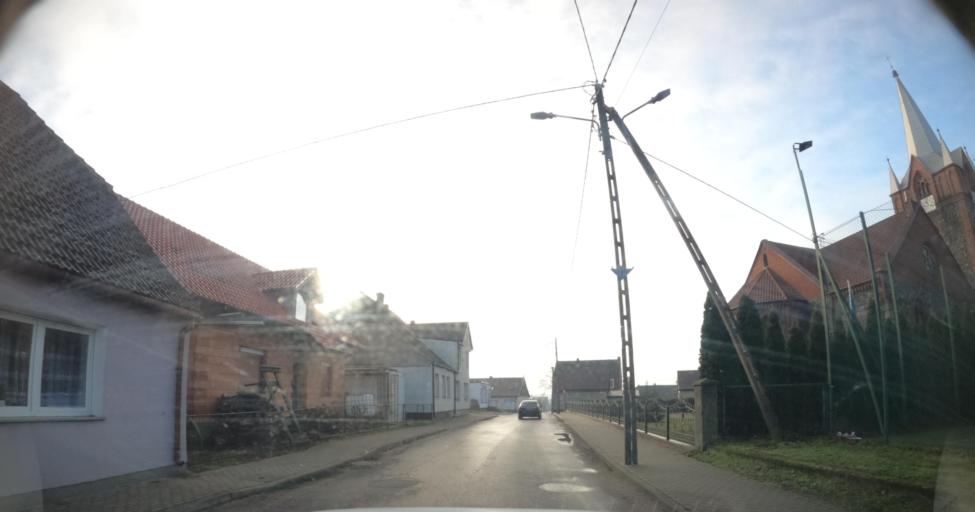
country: PL
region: West Pomeranian Voivodeship
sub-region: Powiat mysliborski
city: Boleszkowice
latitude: 52.7258
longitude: 14.5692
